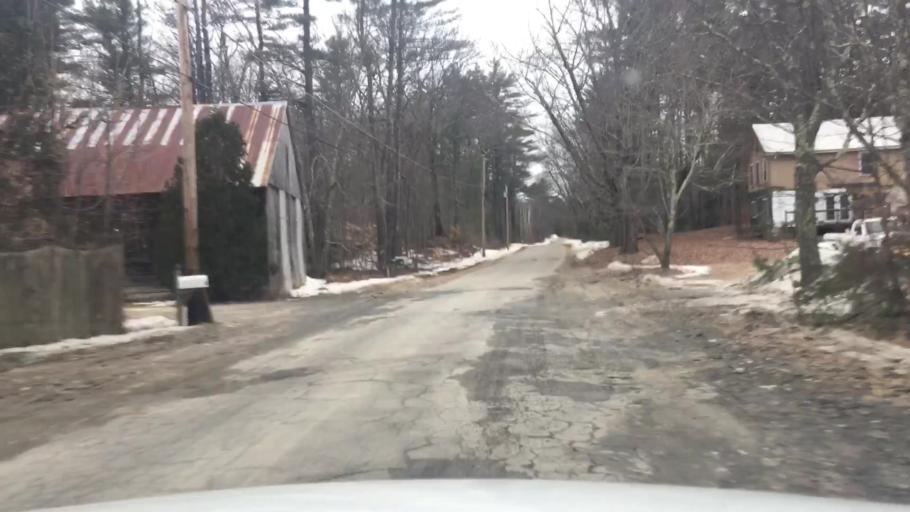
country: US
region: New Hampshire
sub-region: Strafford County
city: Rochester
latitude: 43.3550
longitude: -70.9666
